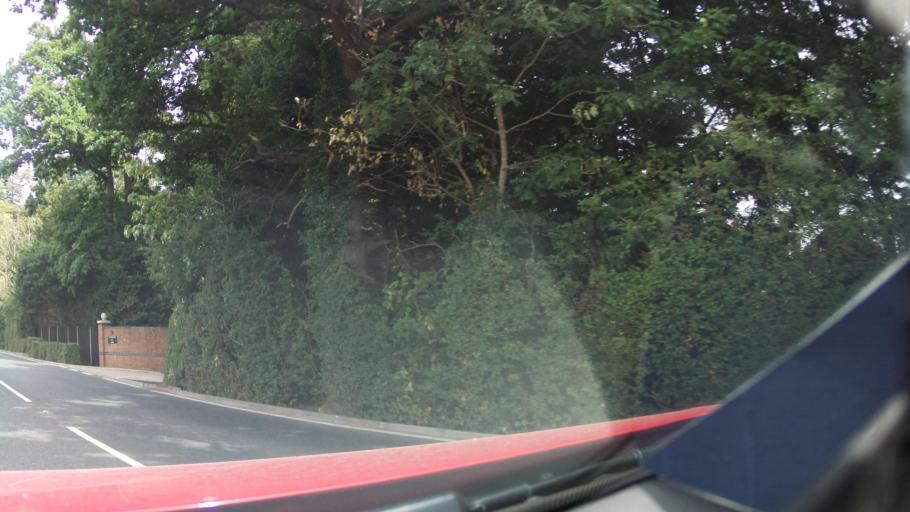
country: GB
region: England
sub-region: Surrey
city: Salfords
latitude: 51.1982
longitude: -0.1980
